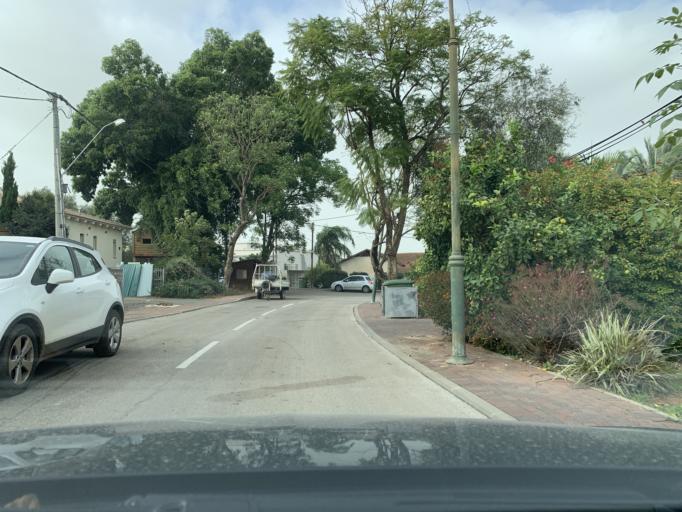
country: IL
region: Central District
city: Jaljulya
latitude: 32.1600
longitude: 34.9413
